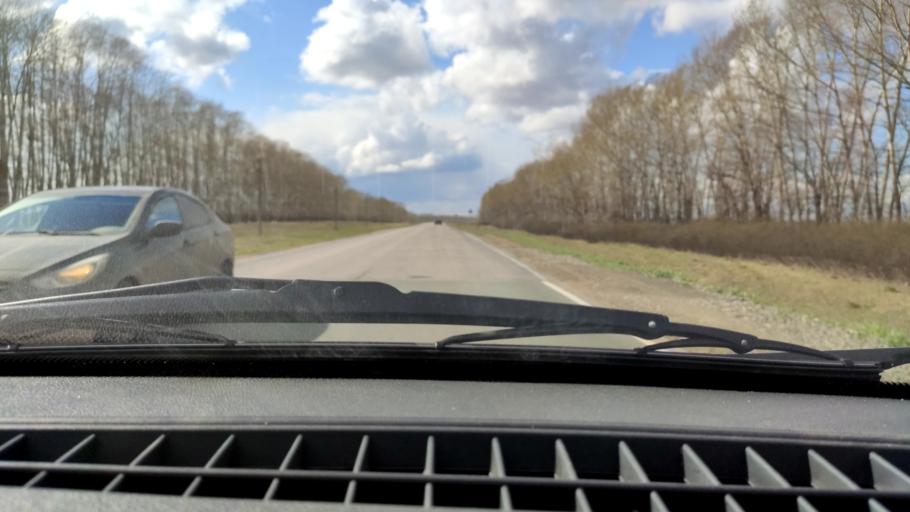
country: RU
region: Bashkortostan
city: Alekseyevka
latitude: 55.0613
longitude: 55.1048
